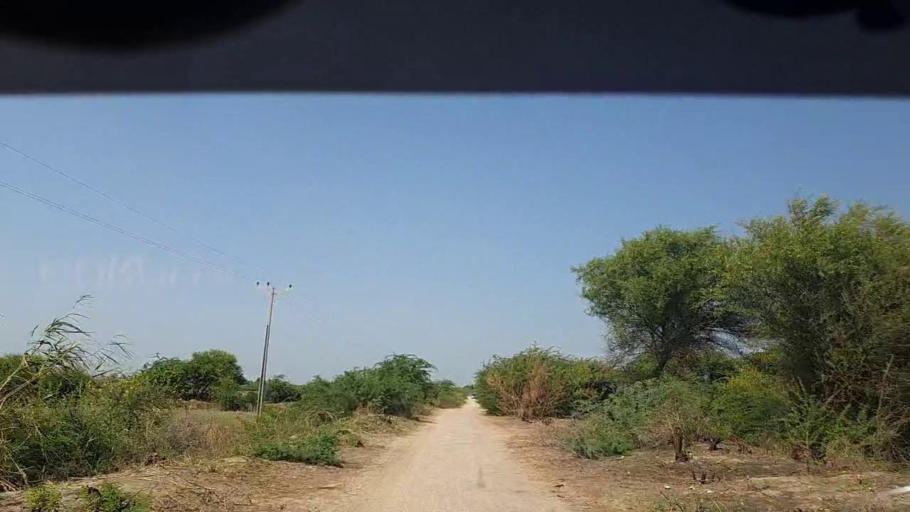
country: PK
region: Sindh
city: Badin
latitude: 24.4647
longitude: 68.7797
